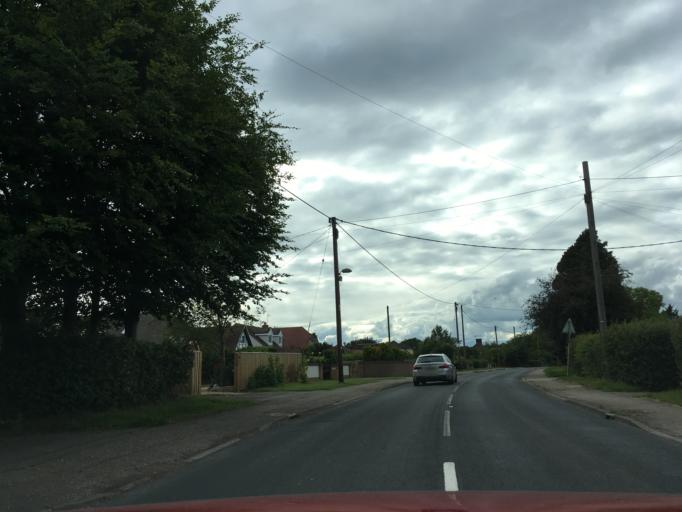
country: GB
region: England
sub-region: Oxfordshire
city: Boars Hill
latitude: 51.7074
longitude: -1.3199
